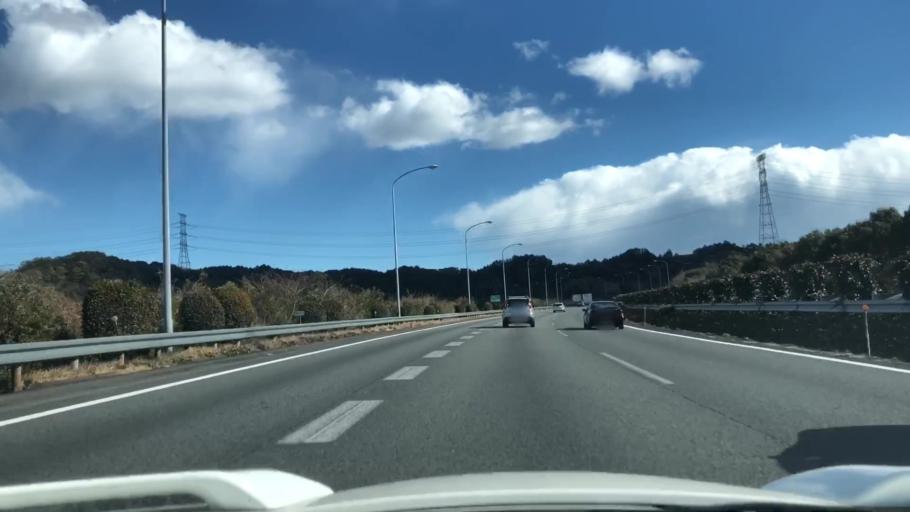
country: JP
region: Shizuoka
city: Kanaya
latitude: 34.7553
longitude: 138.1178
